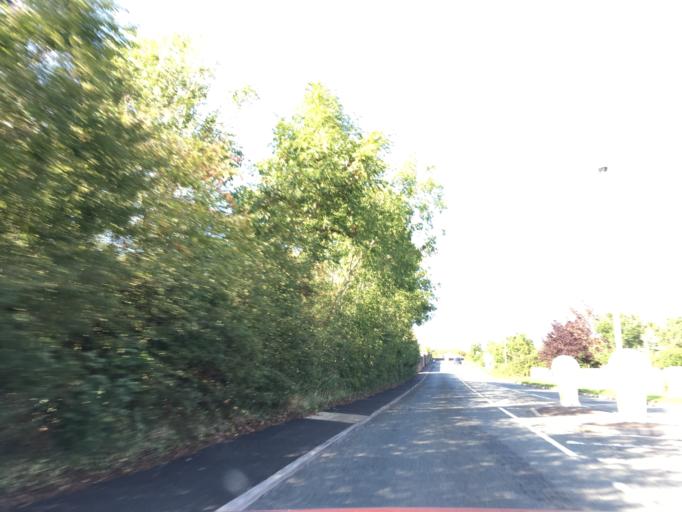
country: GB
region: England
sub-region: Somerset
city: Mendip
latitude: 51.2172
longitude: -2.6170
